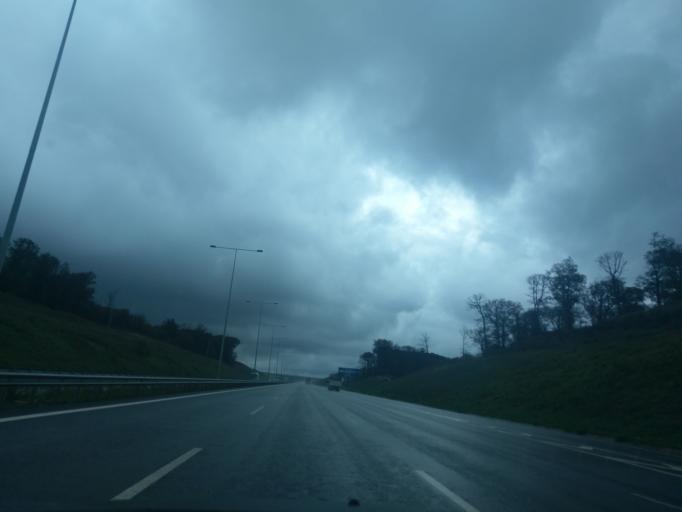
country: TR
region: Istanbul
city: Kemerburgaz
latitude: 41.2354
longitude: 28.8926
